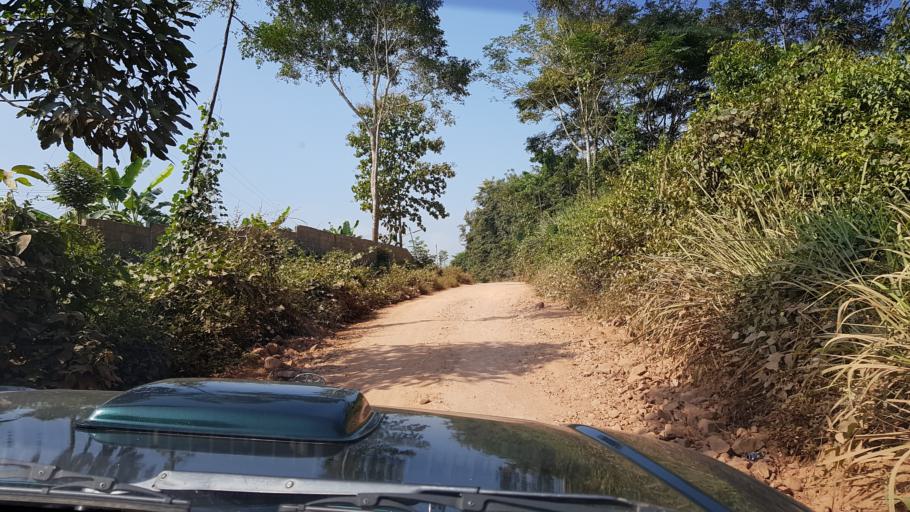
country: LA
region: Oudomxai
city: Muang Xay
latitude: 20.7207
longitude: 102.0477
